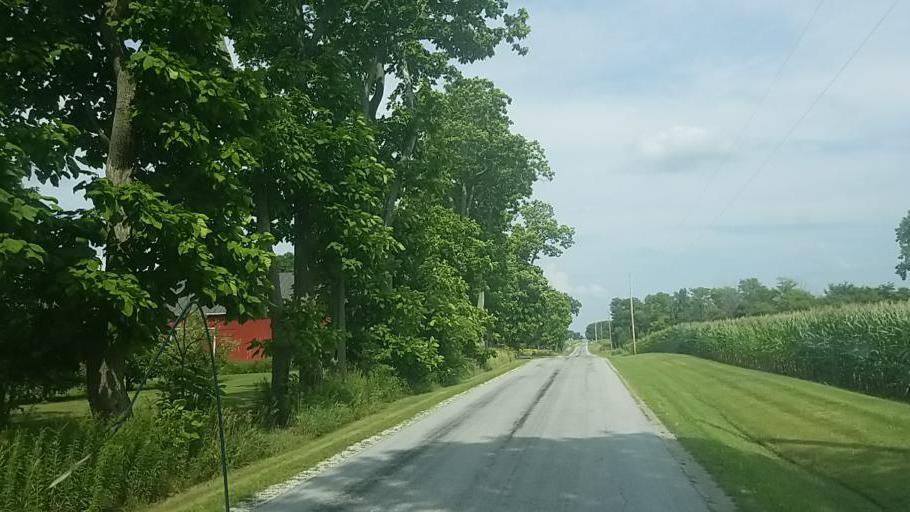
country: US
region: Ohio
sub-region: Hardin County
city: Forest
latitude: 40.8176
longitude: -83.4528
